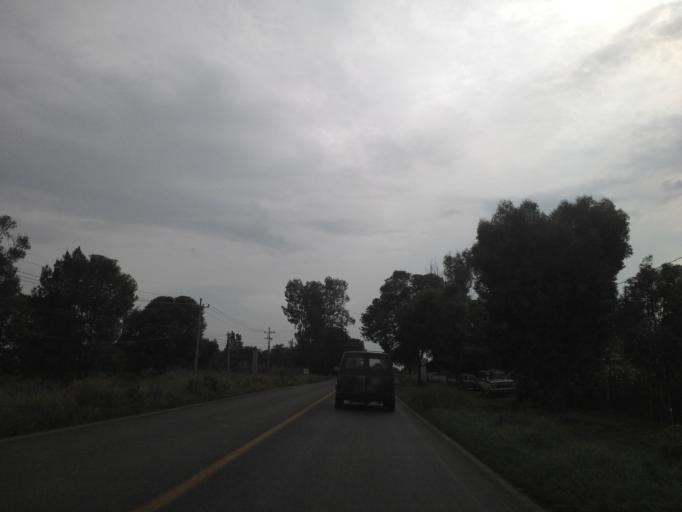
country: MX
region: Jalisco
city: Tepatitlan de Morelos
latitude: 20.7684
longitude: -102.8057
